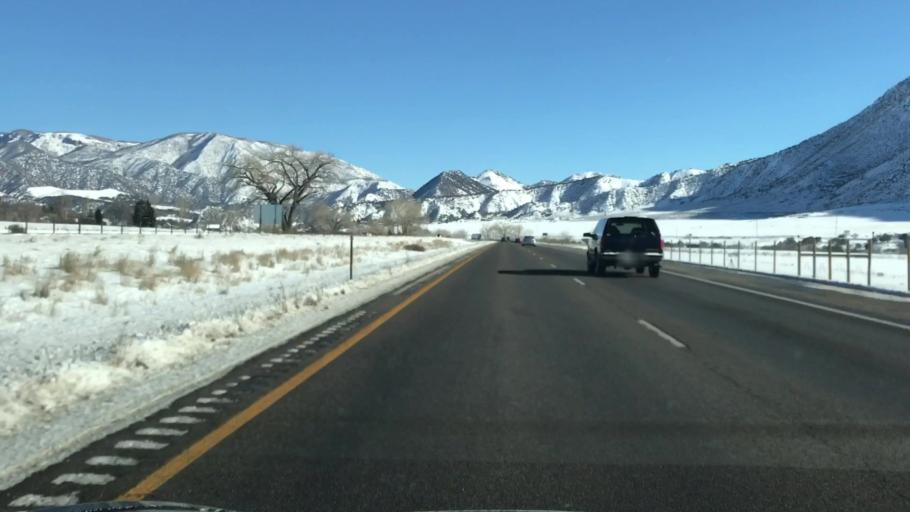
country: US
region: Colorado
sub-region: Garfield County
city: New Castle
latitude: 39.5658
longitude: -107.4985
